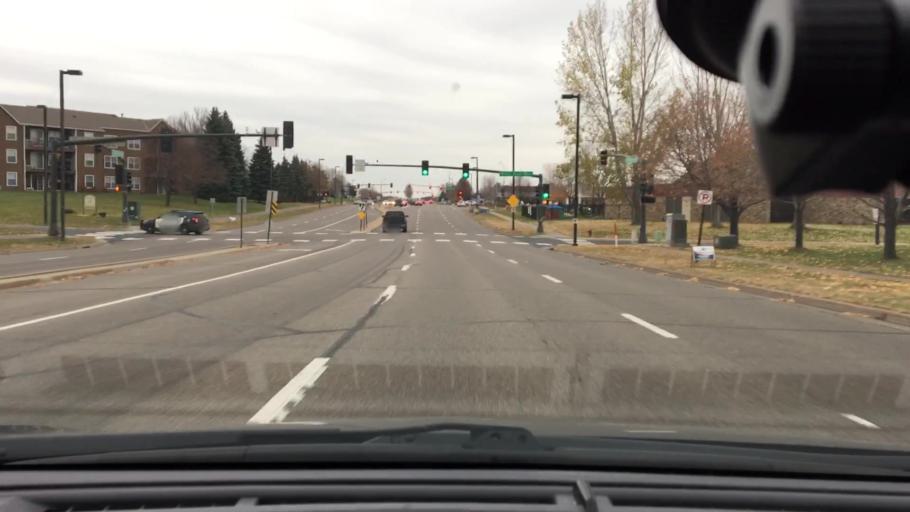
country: US
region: Minnesota
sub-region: Hennepin County
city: Maple Grove
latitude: 45.1075
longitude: -93.4519
